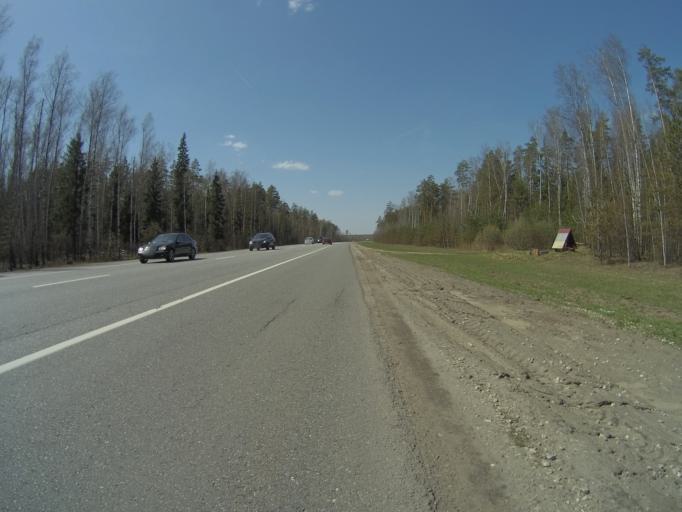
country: RU
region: Vladimir
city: Raduzhnyy
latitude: 56.0649
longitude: 40.3291
